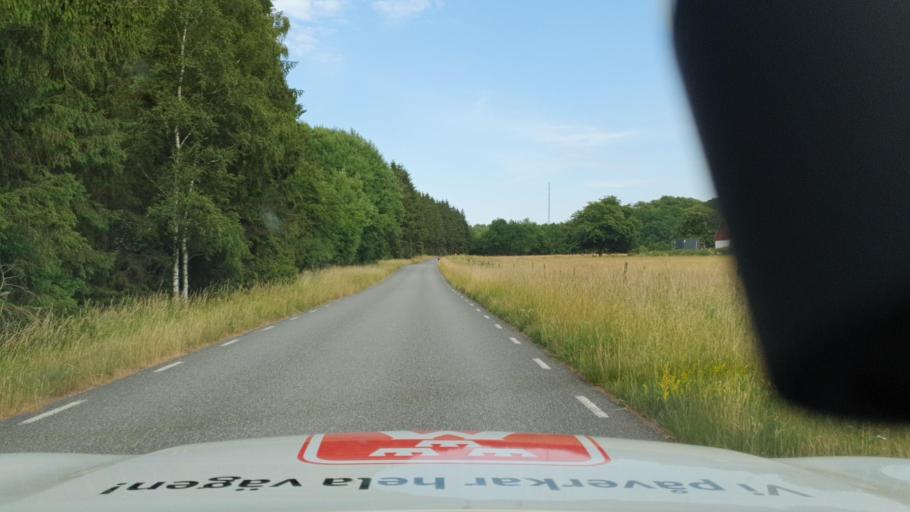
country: SE
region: Skane
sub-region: Kristianstads Kommun
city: Degeberga
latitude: 55.7005
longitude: 14.0489
